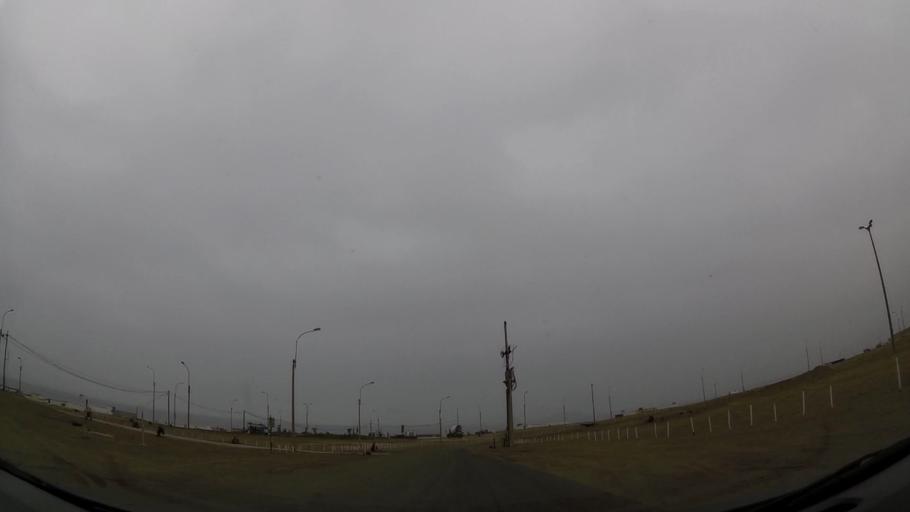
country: PE
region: Lima
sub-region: Lima
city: Punta Hermosa
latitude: -12.3234
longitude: -76.8355
